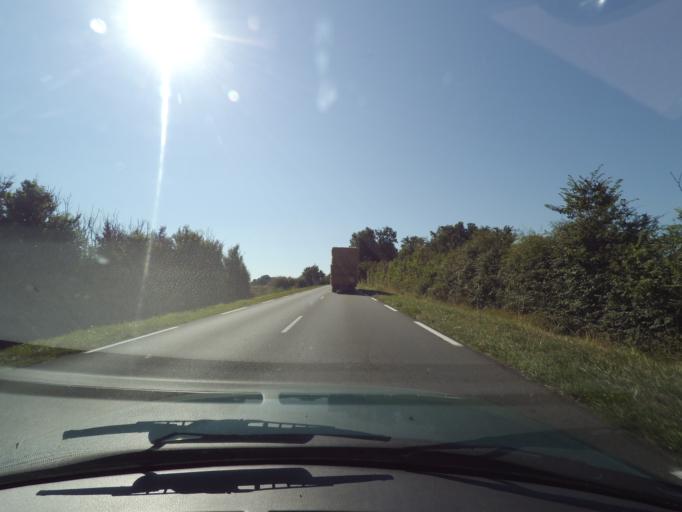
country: FR
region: Poitou-Charentes
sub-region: Departement de la Vienne
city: Lussac-les-Chateaux
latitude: 46.3904
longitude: 0.7392
